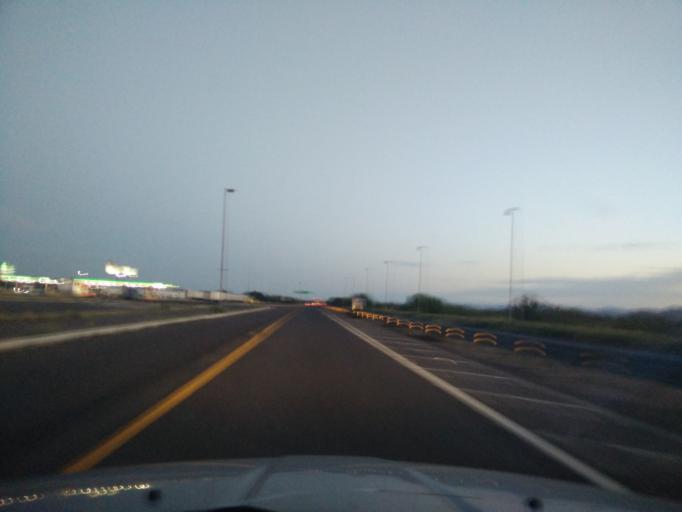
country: MX
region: Sonora
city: Heroica Guaymas
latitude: 28.0414
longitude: -110.9382
